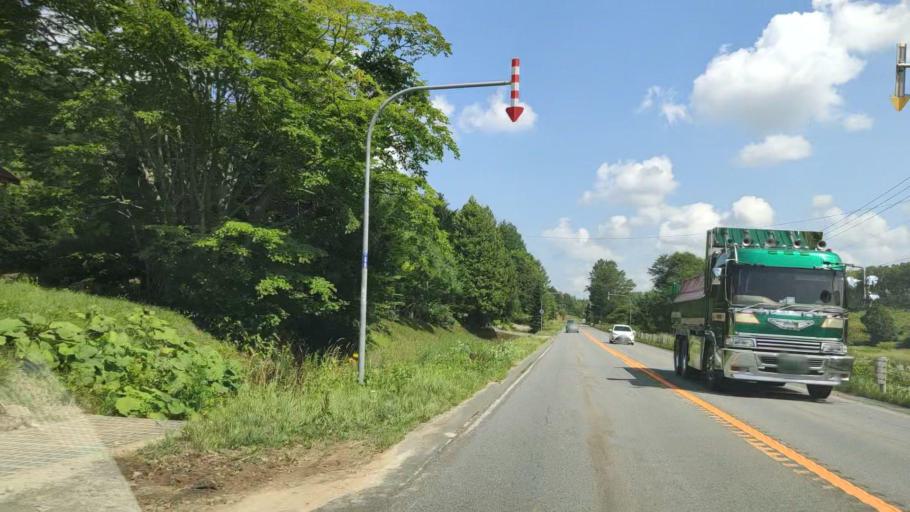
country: JP
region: Hokkaido
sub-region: Asahikawa-shi
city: Asahikawa
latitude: 43.5688
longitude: 142.4361
